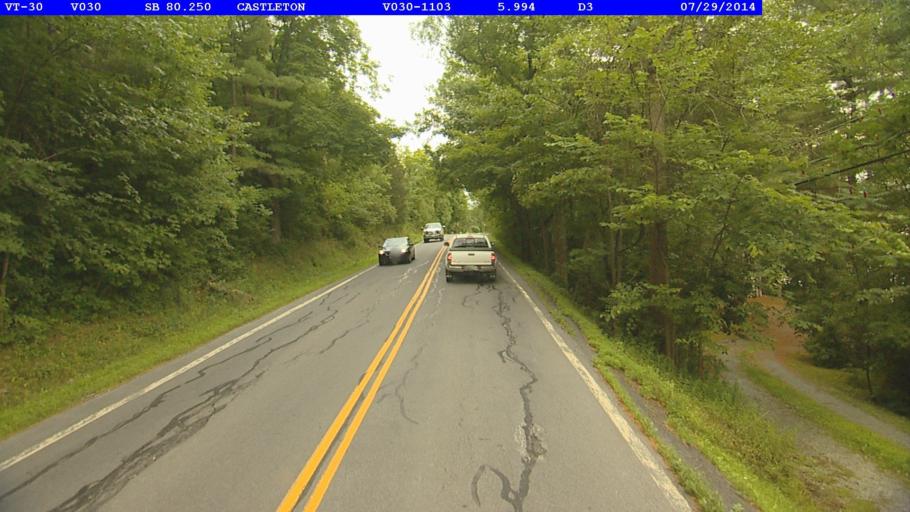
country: US
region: Vermont
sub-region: Rutland County
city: Castleton
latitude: 43.6710
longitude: -73.1916
